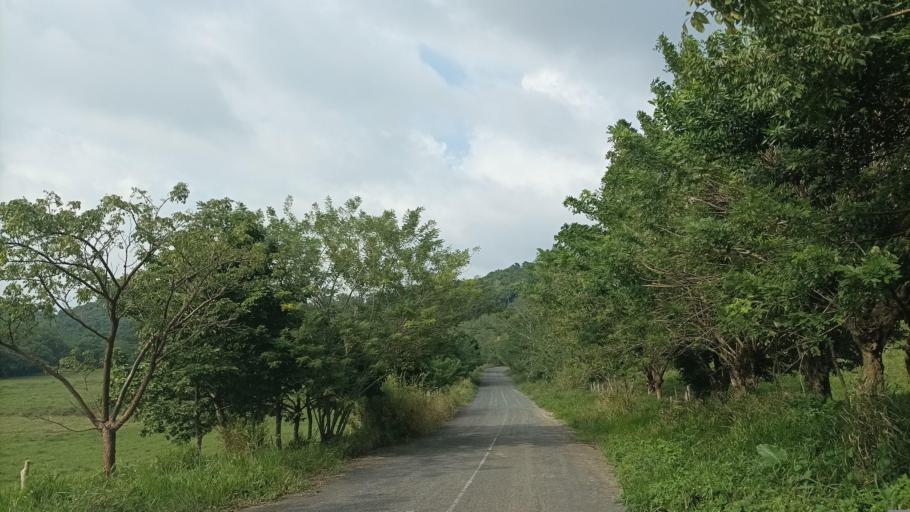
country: MX
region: Veracruz
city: Allende
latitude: 18.1157
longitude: -94.2913
